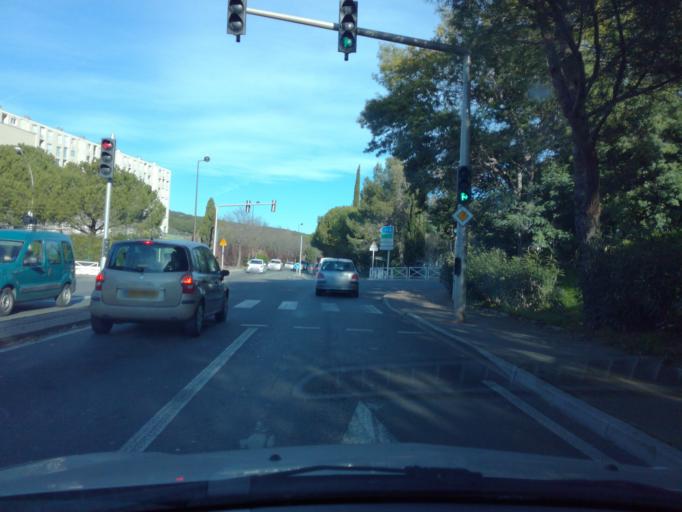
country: FR
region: Provence-Alpes-Cote d'Azur
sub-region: Departement des Alpes-Maritimes
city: Vallauris
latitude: 43.5761
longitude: 7.0903
